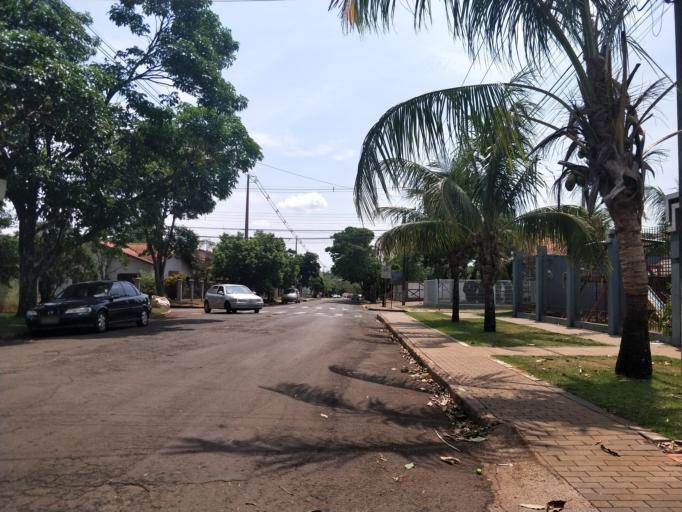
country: BR
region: Parana
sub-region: Marechal Candido Rondon
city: Marechal Candido Rondon
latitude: -24.5602
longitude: -54.0503
